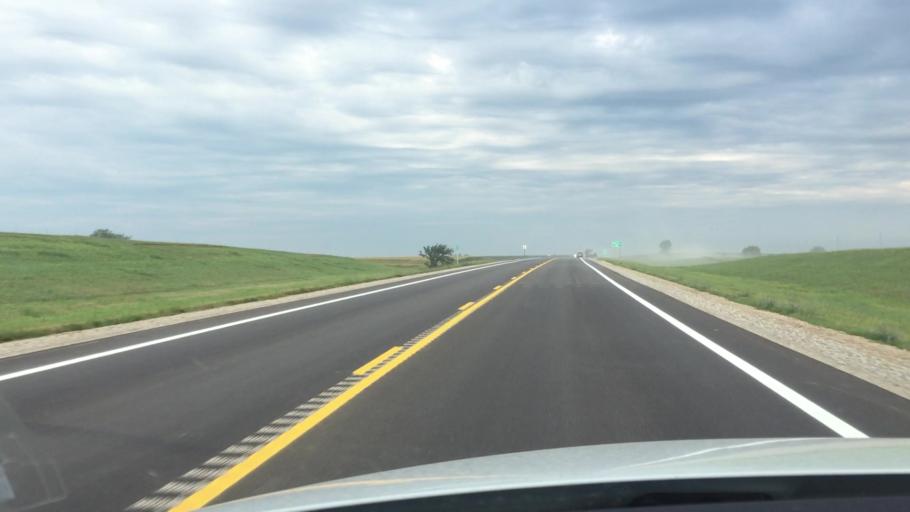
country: US
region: Kansas
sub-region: Brown County
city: Hiawatha
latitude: 39.8412
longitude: -95.4068
